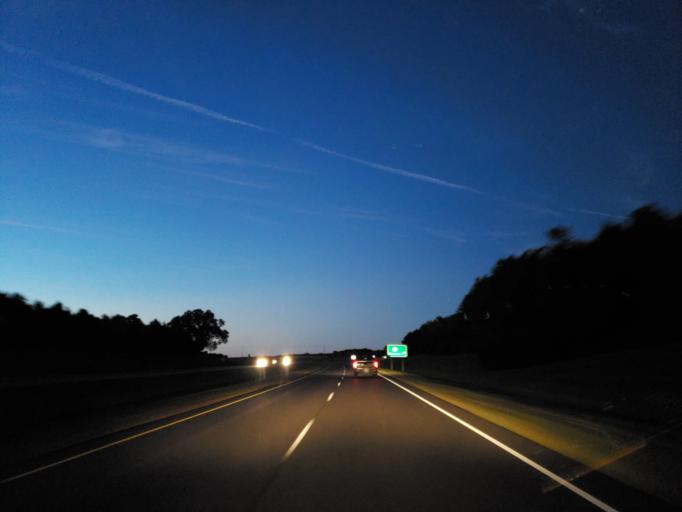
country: US
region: Mississippi
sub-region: Clarke County
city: Quitman
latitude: 32.0529
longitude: -88.6767
